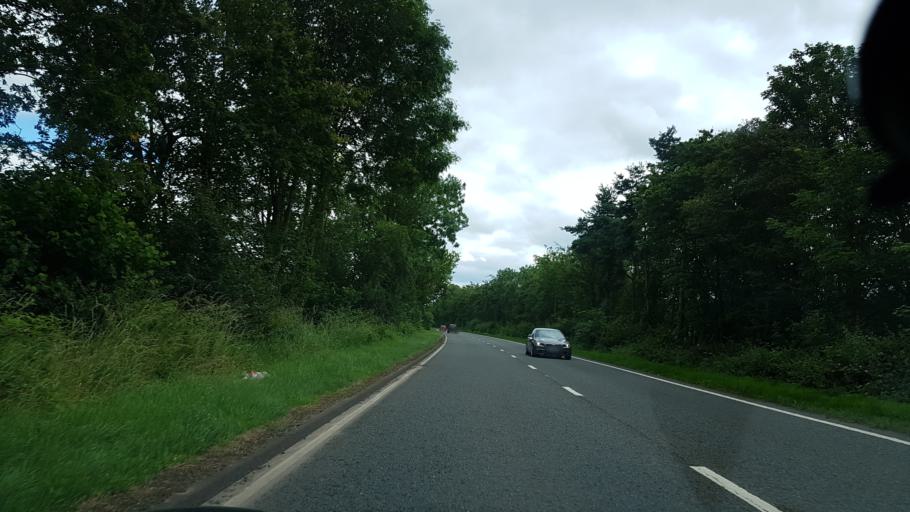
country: GB
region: Wales
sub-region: Monmouthshire
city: Abergavenny
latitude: 51.8185
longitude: -3.0082
